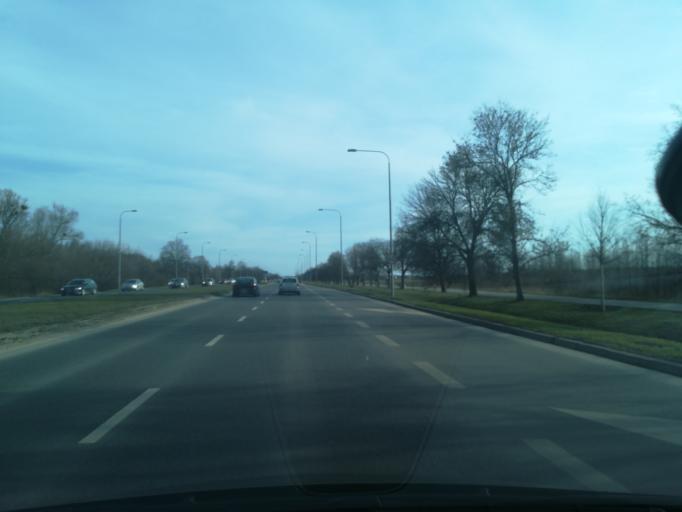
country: PL
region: Masovian Voivodeship
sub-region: Warszawa
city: Wilanow
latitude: 52.1469
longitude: 21.0934
